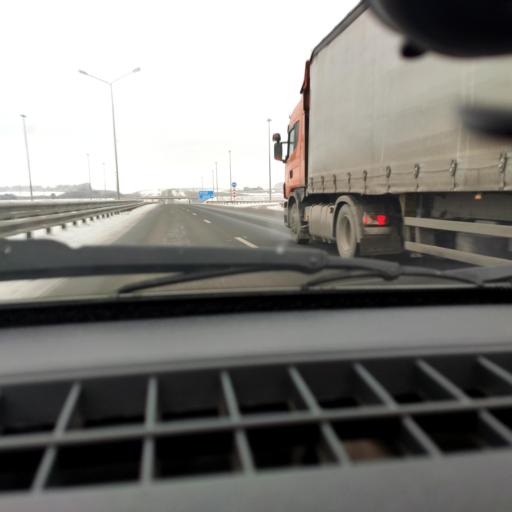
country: RU
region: Bashkortostan
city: Kushnarenkovo
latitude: 55.0757
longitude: 55.2816
